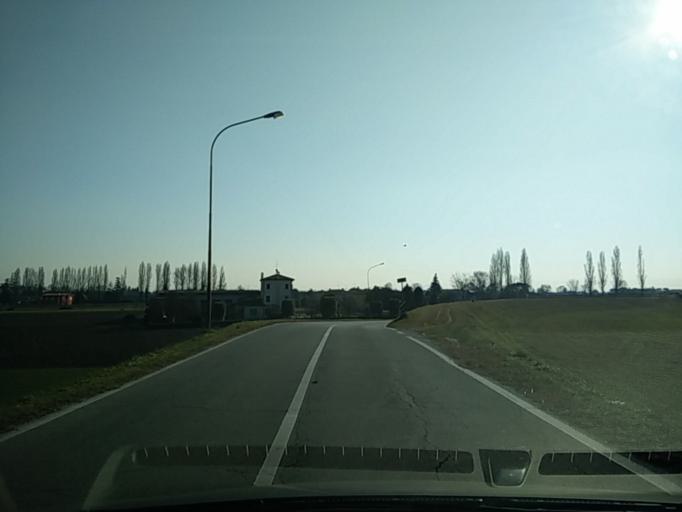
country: IT
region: Veneto
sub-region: Provincia di Venezia
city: Torre di Mosto
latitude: 45.6926
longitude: 12.7146
